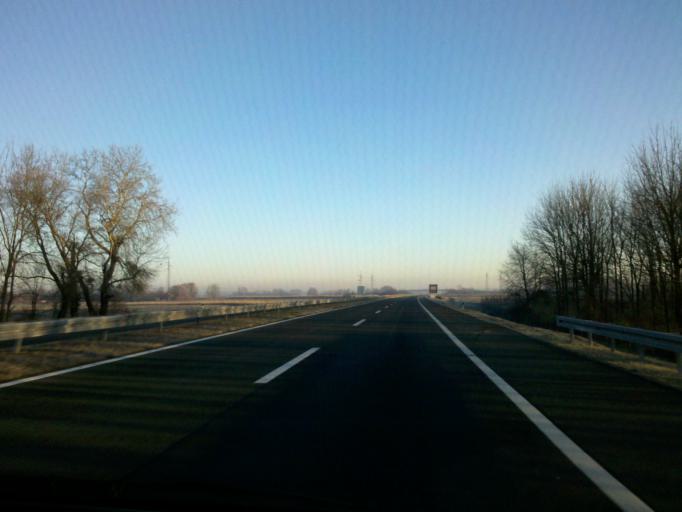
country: HR
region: Medimurska
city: Orehovica
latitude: 46.3184
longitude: 16.5125
